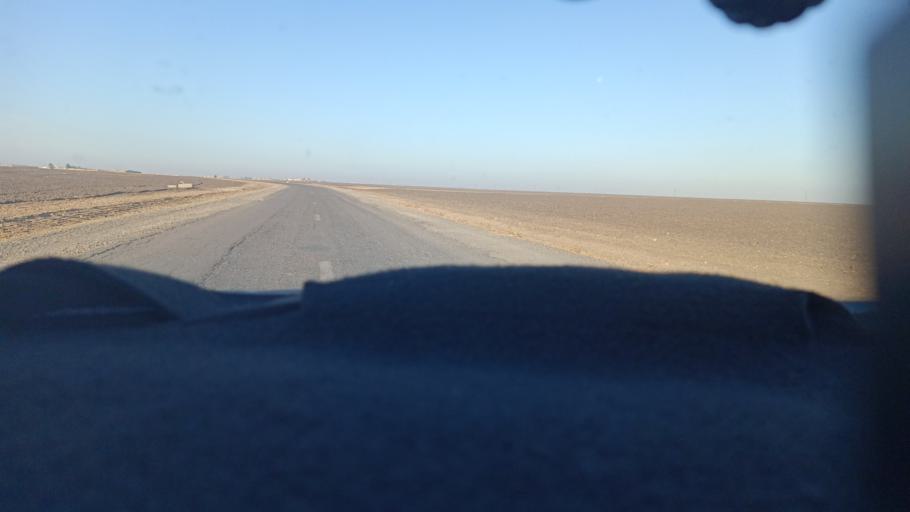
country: MA
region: Doukkala-Abda
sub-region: Safi
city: Youssoufia
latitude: 32.3676
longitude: -8.7427
